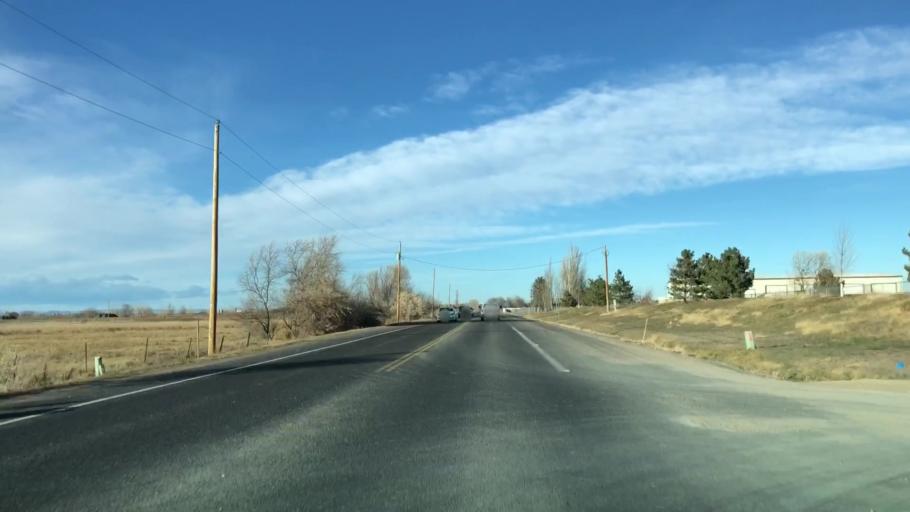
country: US
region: Colorado
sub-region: Weld County
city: Windsor
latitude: 40.4948
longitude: -104.9819
